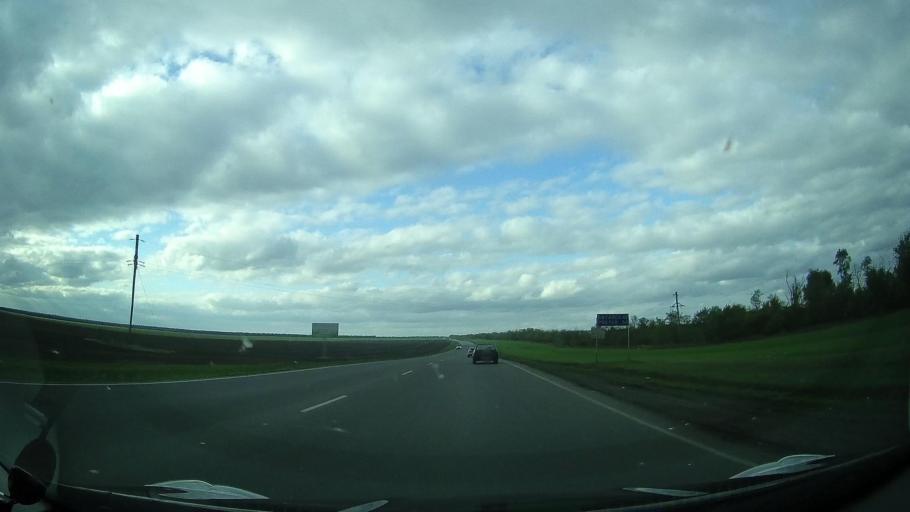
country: RU
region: Rostov
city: Kagal'nitskaya
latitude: 46.8944
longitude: 40.1283
